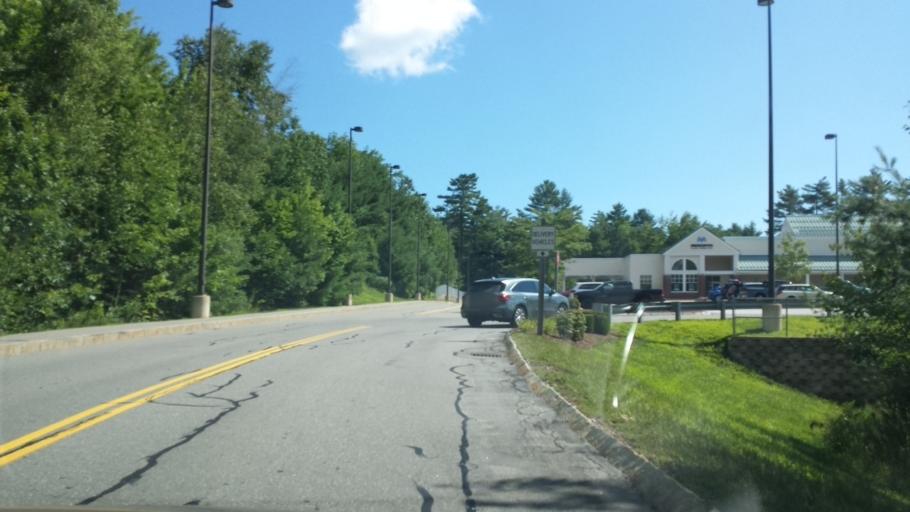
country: US
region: New Hampshire
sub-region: Strafford County
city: New Durham
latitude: 43.4538
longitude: -71.2128
